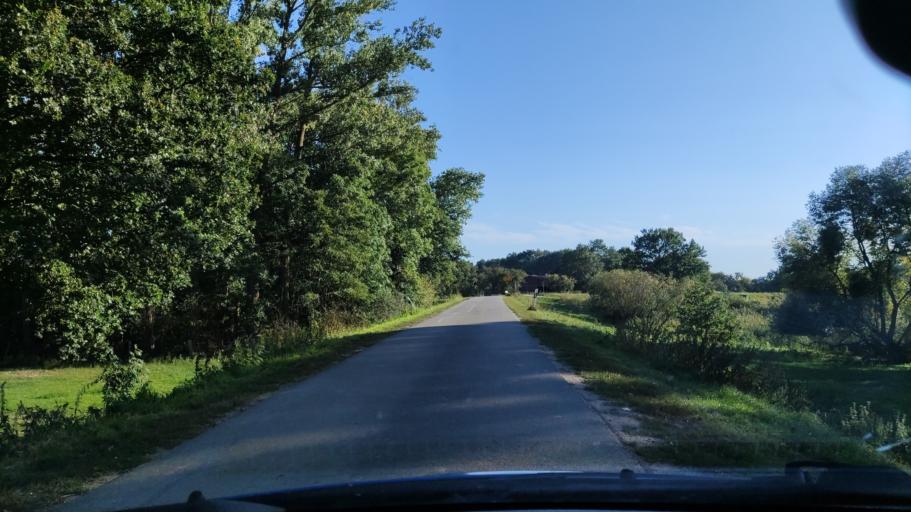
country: DE
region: Lower Saxony
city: Dannenberg
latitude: 53.1230
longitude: 11.0979
